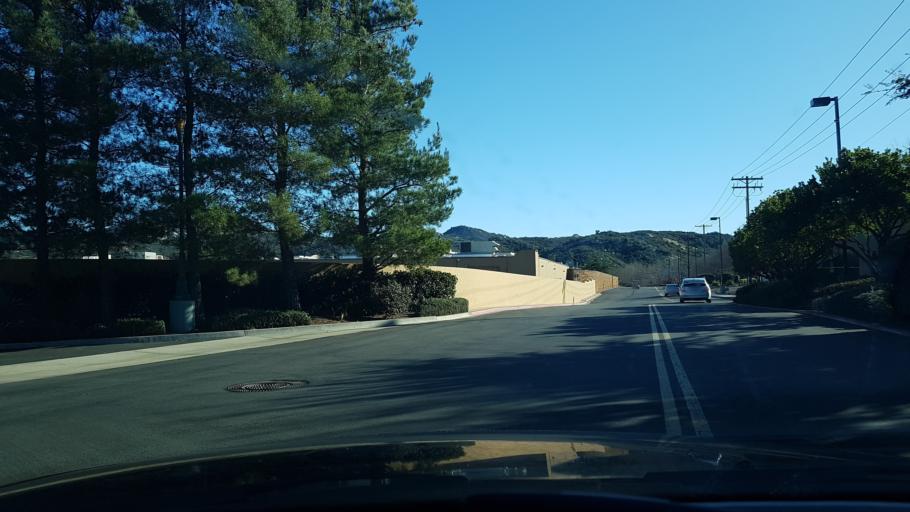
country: US
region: California
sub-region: San Diego County
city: Eucalyptus Hills
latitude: 32.9384
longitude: -116.8768
